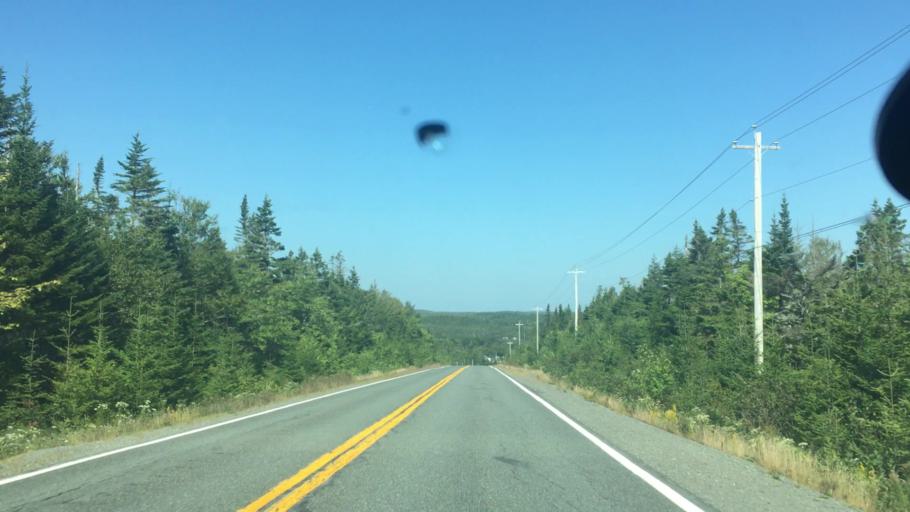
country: CA
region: Nova Scotia
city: Antigonish
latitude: 44.9932
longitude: -62.0974
